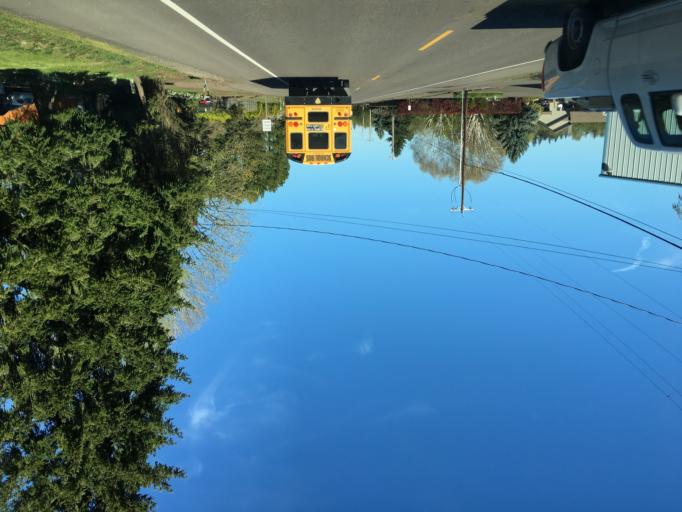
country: US
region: Oregon
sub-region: Marion County
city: Hubbard
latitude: 45.2199
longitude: -122.7616
